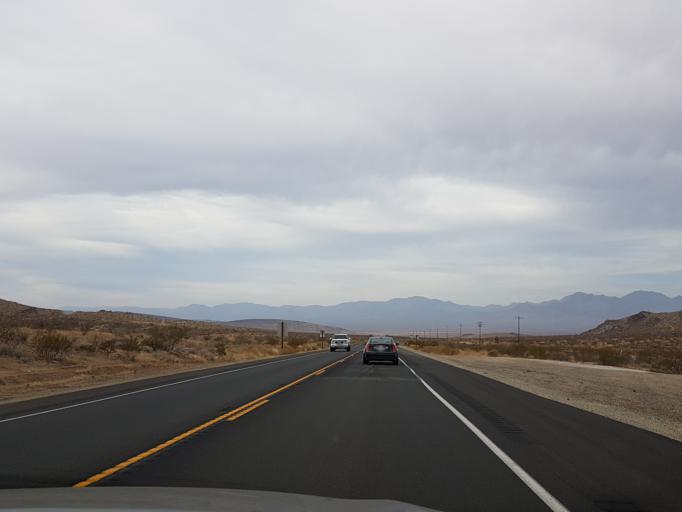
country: US
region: California
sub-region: Kern County
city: Ridgecrest
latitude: 35.5455
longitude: -117.6947
